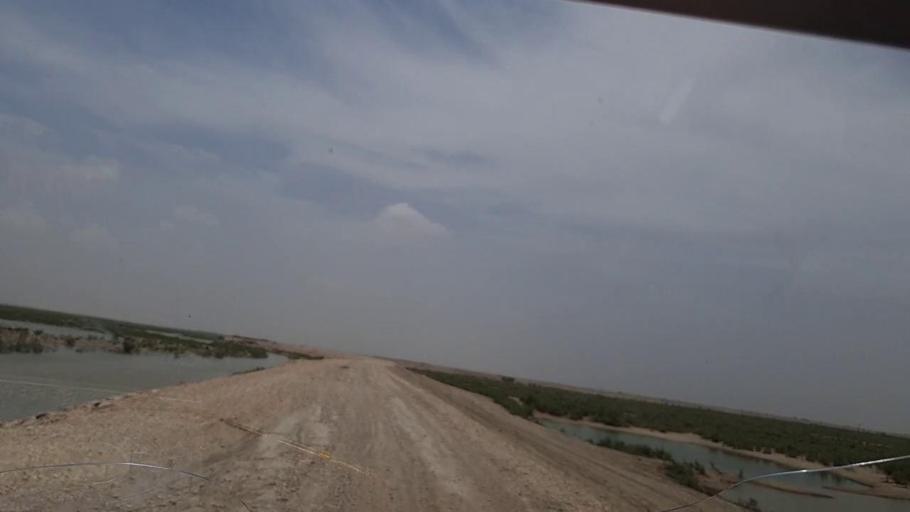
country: PK
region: Sindh
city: Bhan
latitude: 26.5068
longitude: 67.6309
